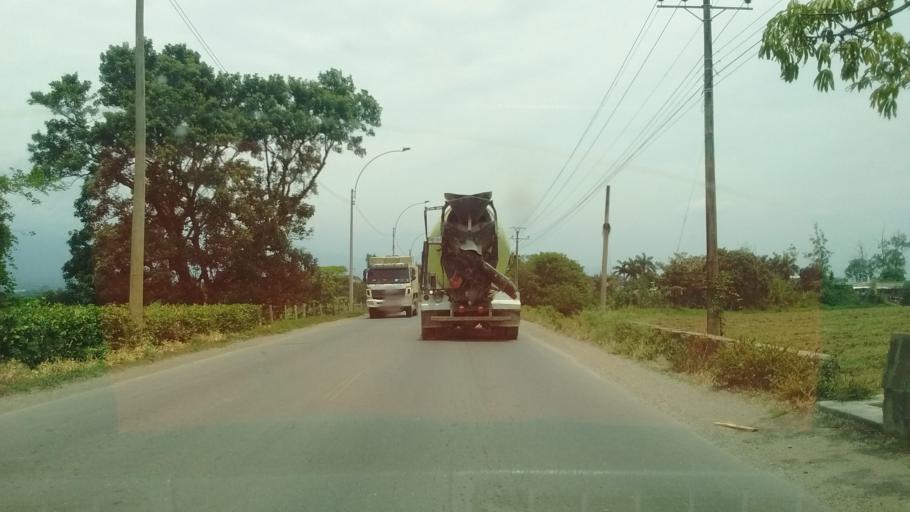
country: CO
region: Valle del Cauca
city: Jamundi
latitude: 3.3119
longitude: -76.4866
